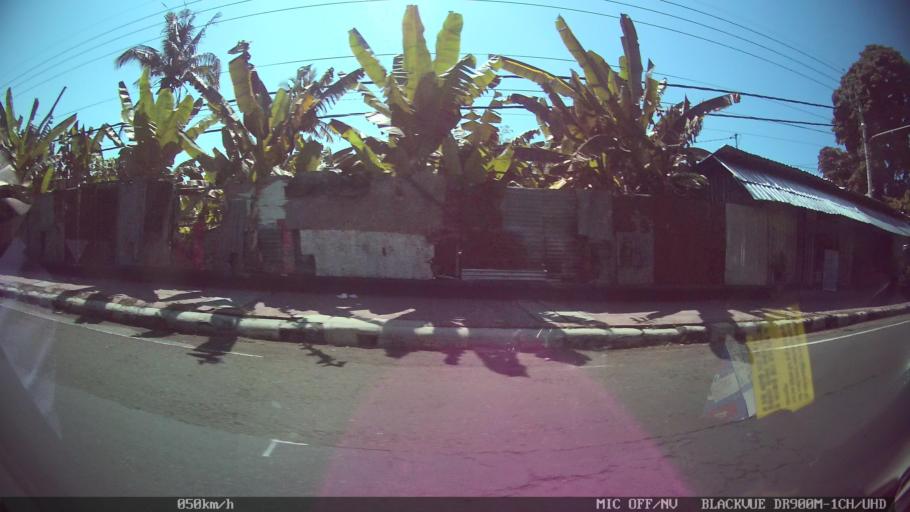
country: ID
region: Bali
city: Banjar Banyualit
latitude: -8.1560
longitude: 115.0350
